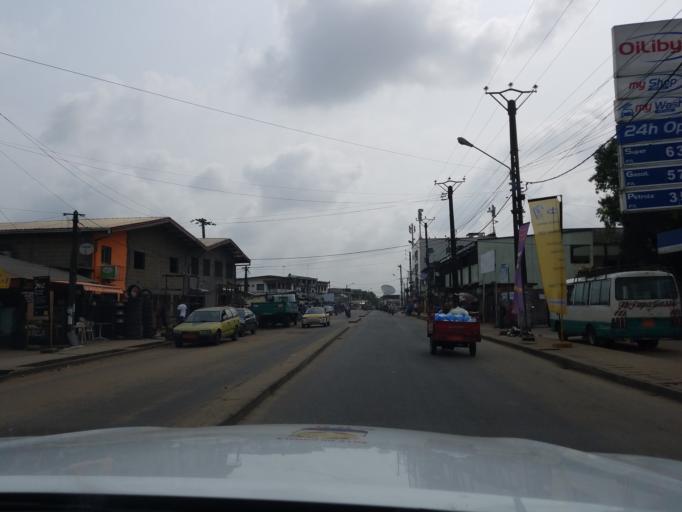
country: CM
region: Littoral
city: Douala
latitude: 4.0639
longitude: 9.7172
